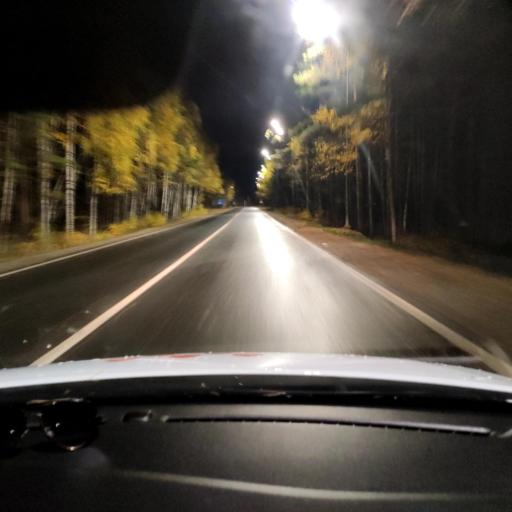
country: RU
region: Tatarstan
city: Verkhniy Uslon
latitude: 55.6374
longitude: 49.0224
